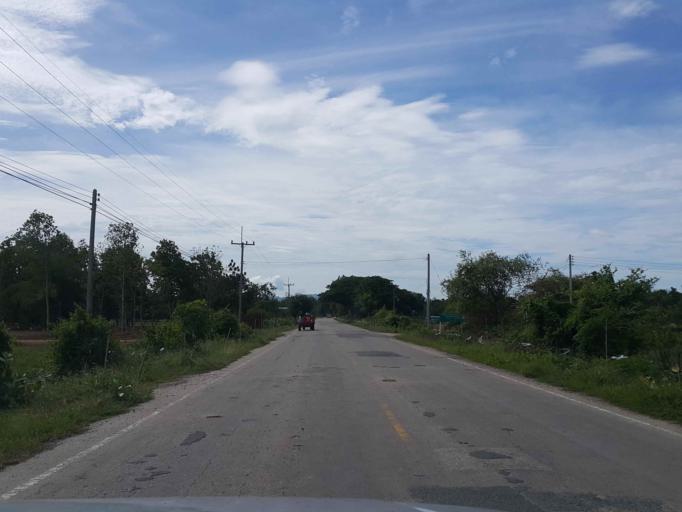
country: TH
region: Sukhothai
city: Ban Dan Lan Hoi
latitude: 17.1220
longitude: 99.5325
